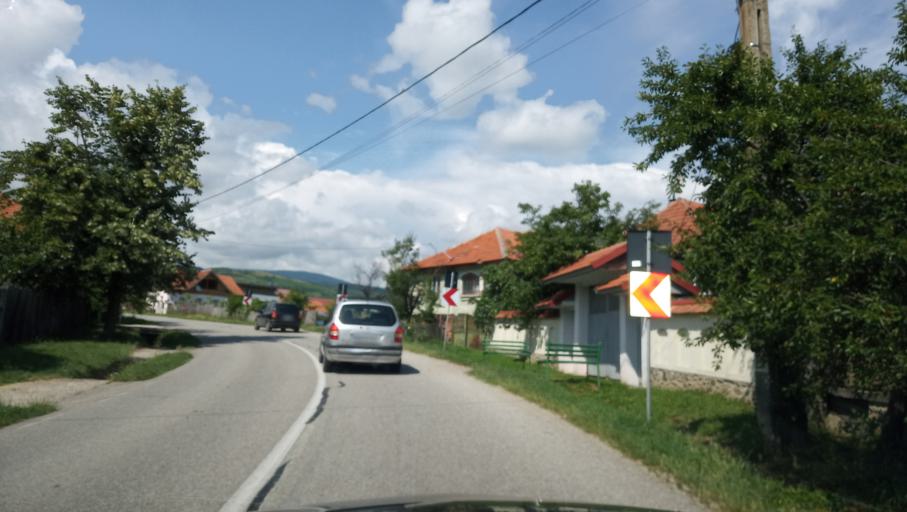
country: RO
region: Gorj
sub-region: Comuna Crasna
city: Crasna
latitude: 45.1677
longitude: 23.4835
